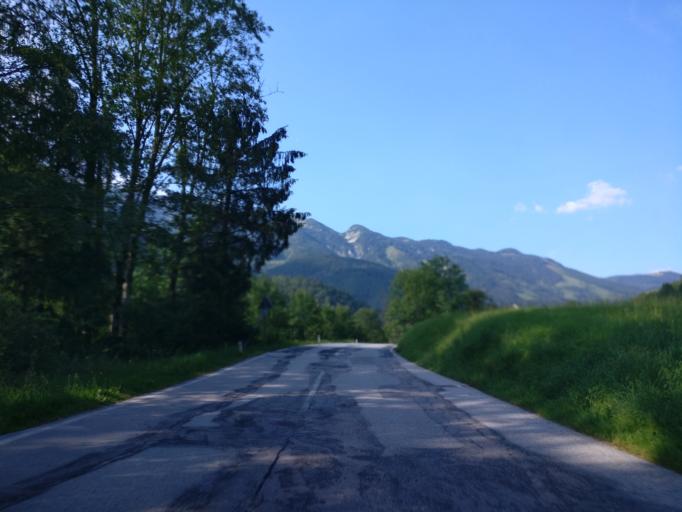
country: AT
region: Styria
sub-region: Politischer Bezirk Liezen
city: Gams bei Hieflau
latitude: 47.6886
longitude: 14.7793
